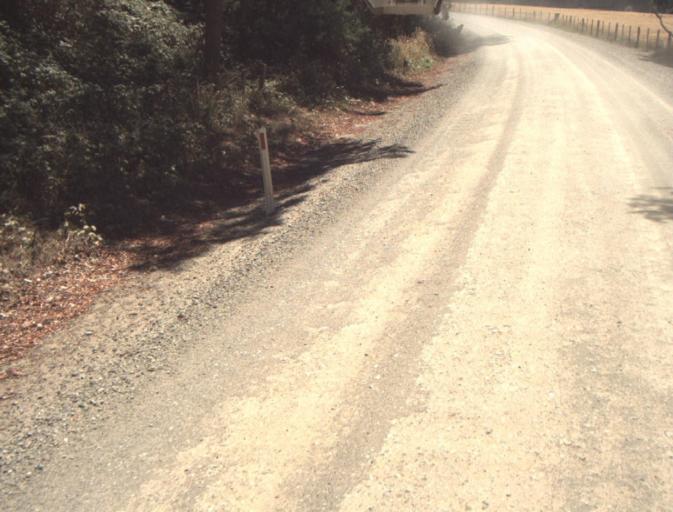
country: AU
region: Tasmania
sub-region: Dorset
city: Scottsdale
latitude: -41.2905
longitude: 147.3925
